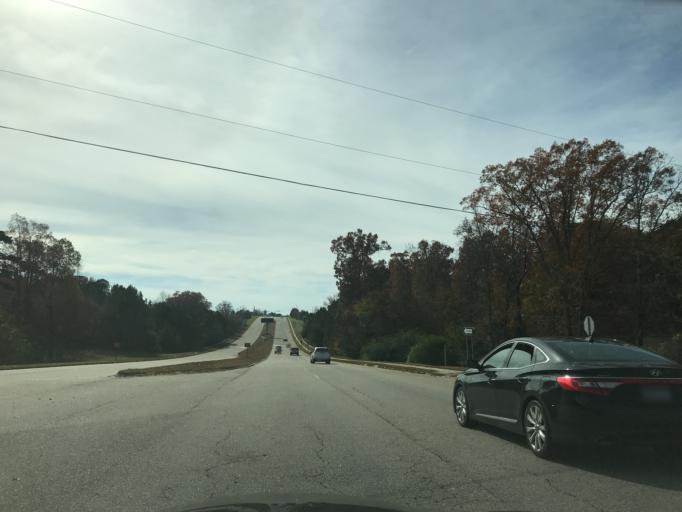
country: US
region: North Carolina
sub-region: Wake County
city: West Raleigh
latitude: 35.8204
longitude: -78.7109
